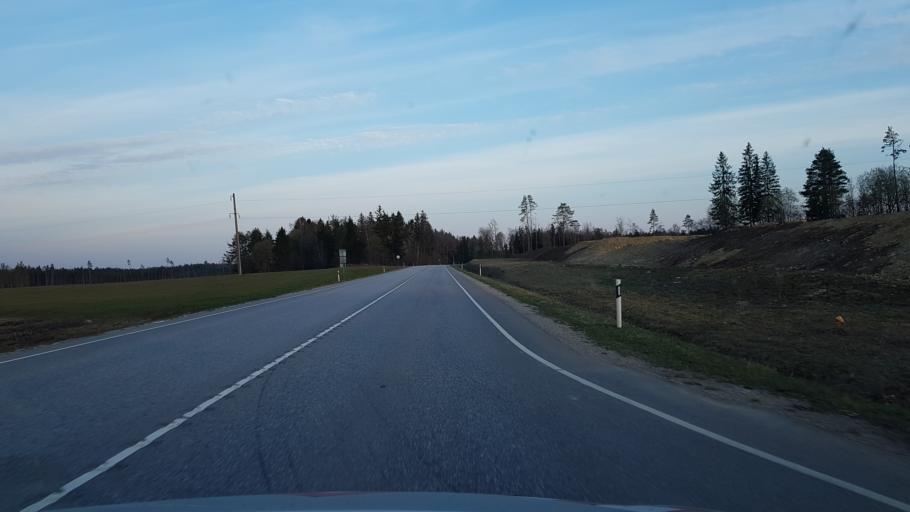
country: EE
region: Laeaene-Virumaa
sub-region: Someru vald
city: Someru
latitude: 59.3457
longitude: 26.4076
